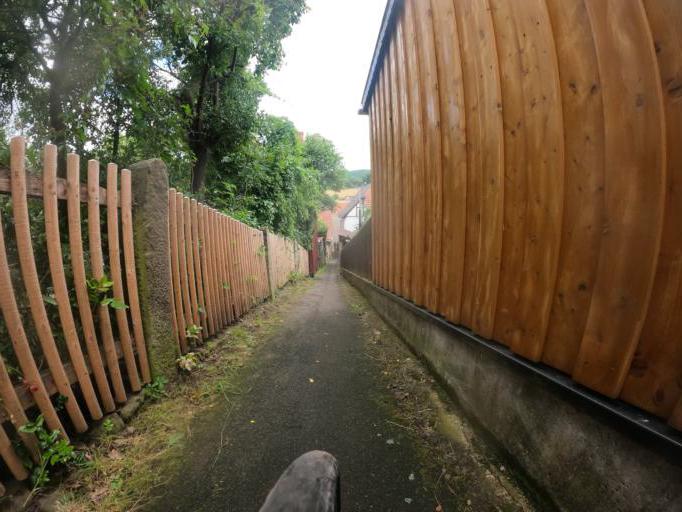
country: DE
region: Thuringia
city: Lindewerra
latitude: 51.3079
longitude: 9.9238
